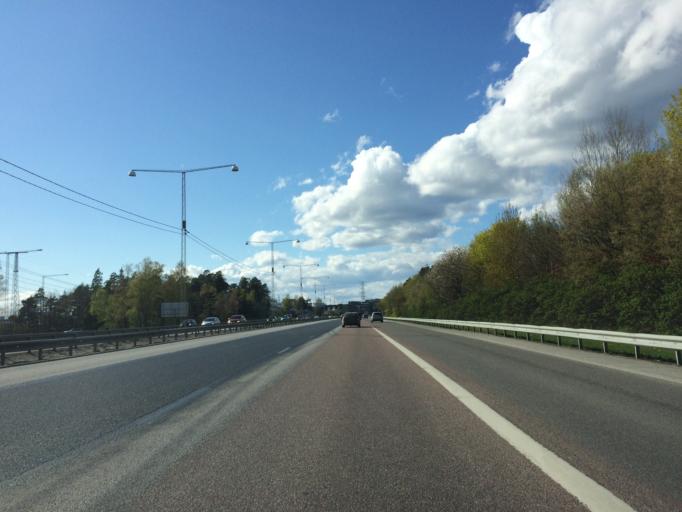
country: SE
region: Stockholm
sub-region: Stockholms Kommun
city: Kista
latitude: 59.4171
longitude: 17.9349
